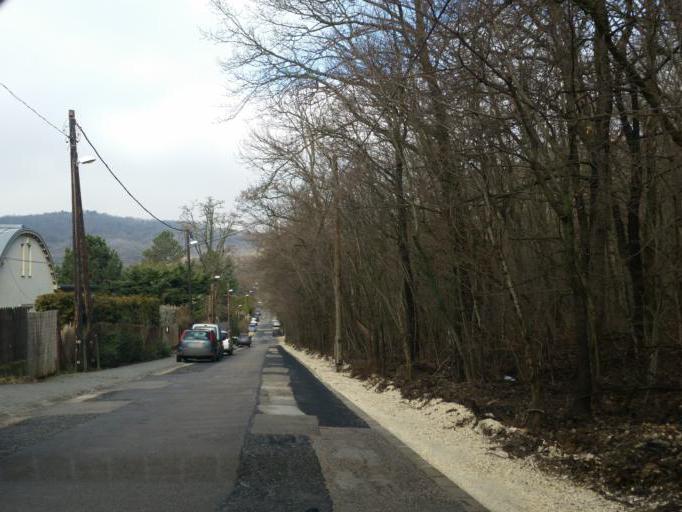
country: HU
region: Budapest
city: Budapest II. keruelet
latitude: 47.5360
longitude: 18.9918
